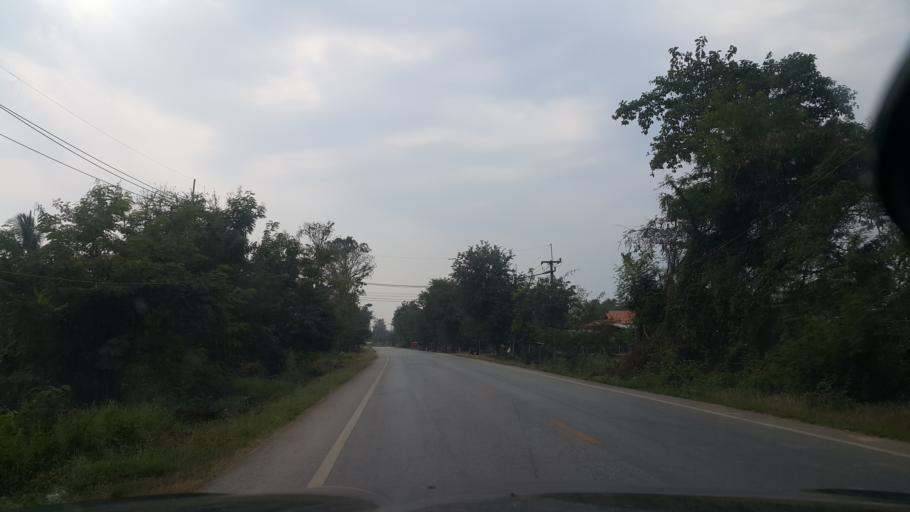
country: TH
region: Sukhothai
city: Si Samrong
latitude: 17.0989
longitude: 99.8855
